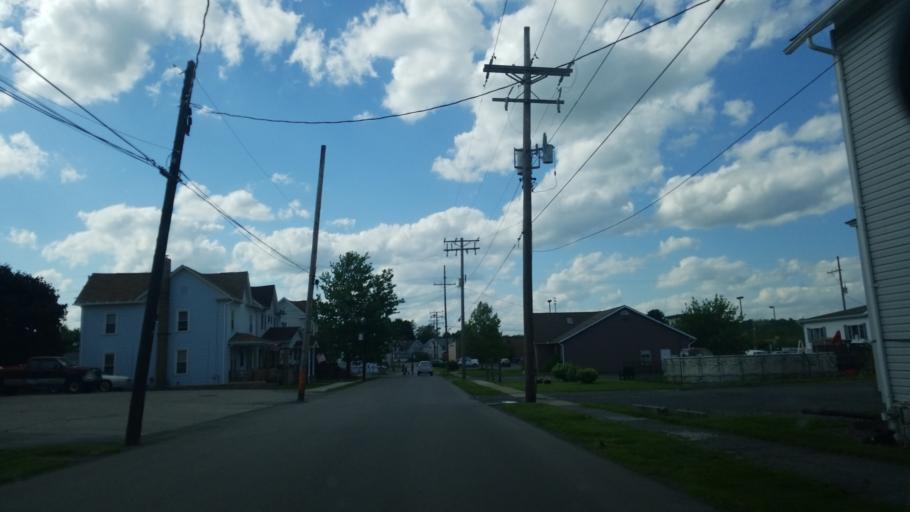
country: US
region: Pennsylvania
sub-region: Centre County
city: Philipsburg
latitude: 40.8994
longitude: -78.2243
